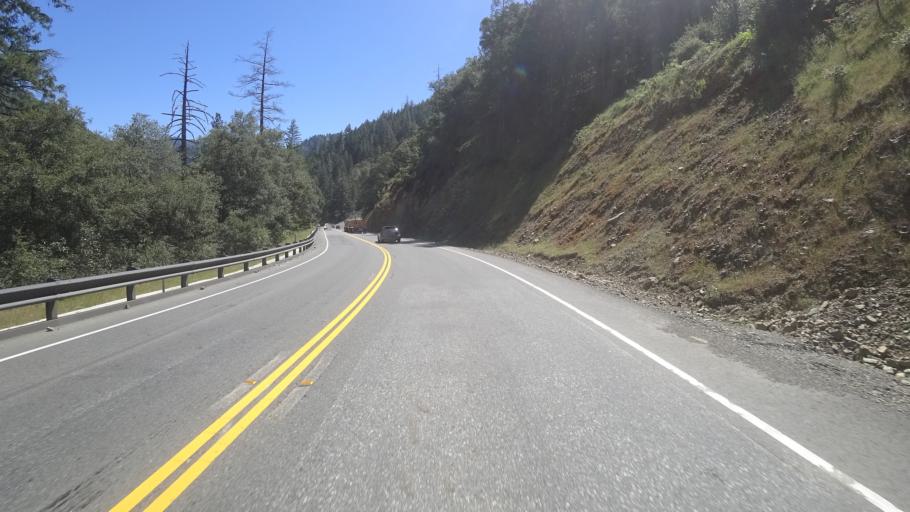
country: US
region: California
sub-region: Humboldt County
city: Willow Creek
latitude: 40.7961
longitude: -123.4608
